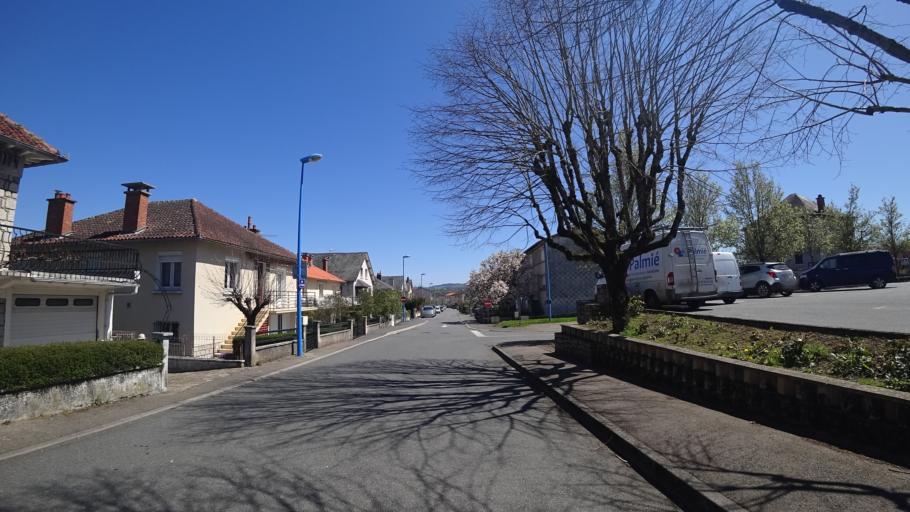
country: FR
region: Midi-Pyrenees
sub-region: Departement de l'Aveyron
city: Rodez
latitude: 44.3636
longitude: 2.5934
